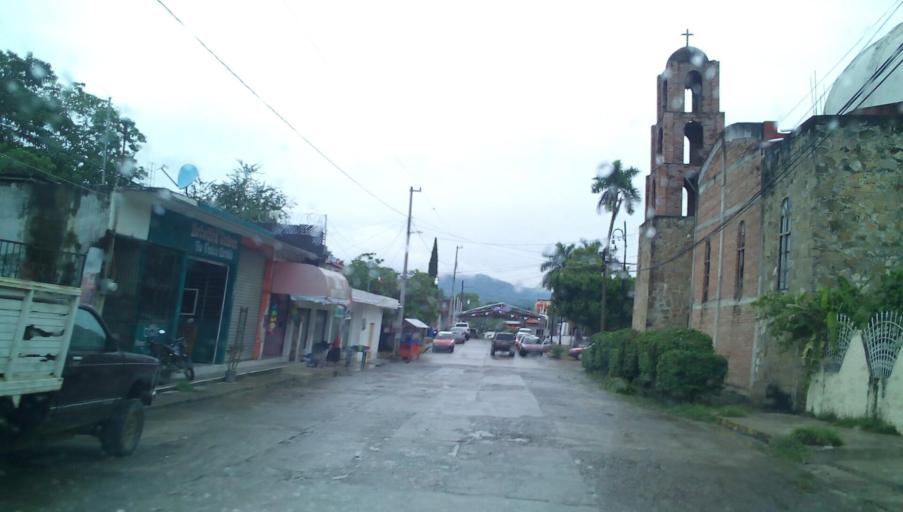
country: MX
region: Veracruz
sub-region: Chalma
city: San Pedro Coyutla
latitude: 21.2077
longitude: -98.3968
